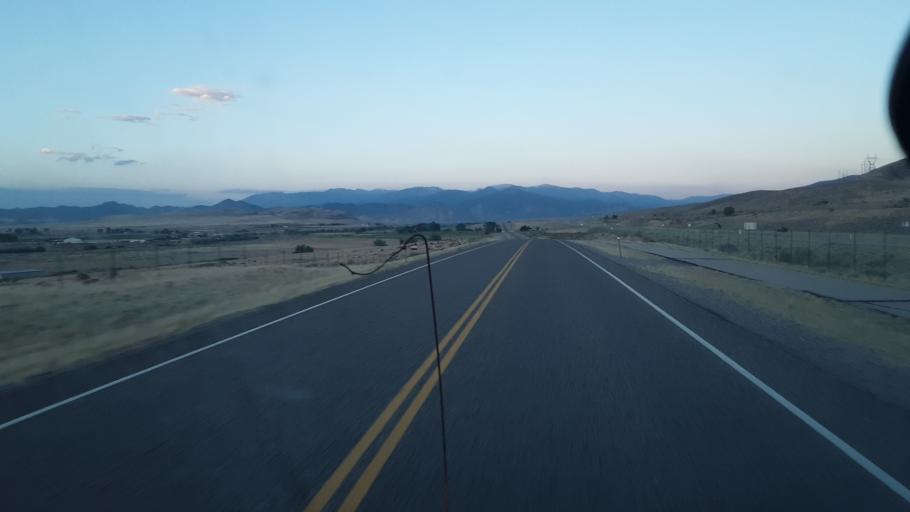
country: US
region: Utah
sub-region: Sevier County
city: Monroe
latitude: 38.6754
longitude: -112.1612
